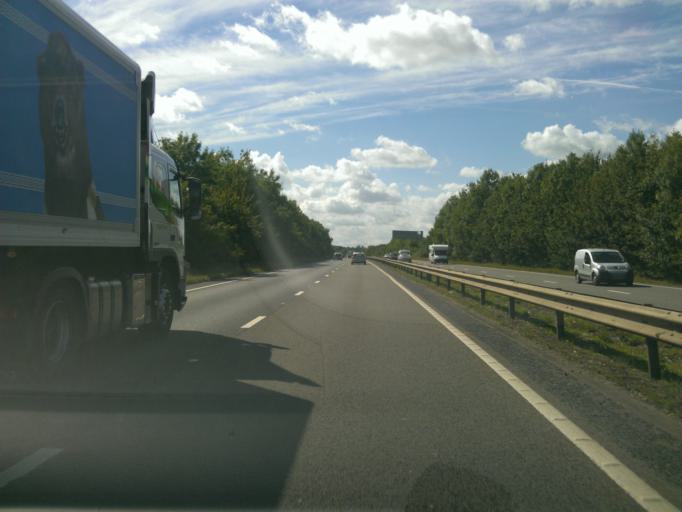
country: GB
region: England
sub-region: Northamptonshire
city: Thrapston
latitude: 52.3924
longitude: -0.5757
